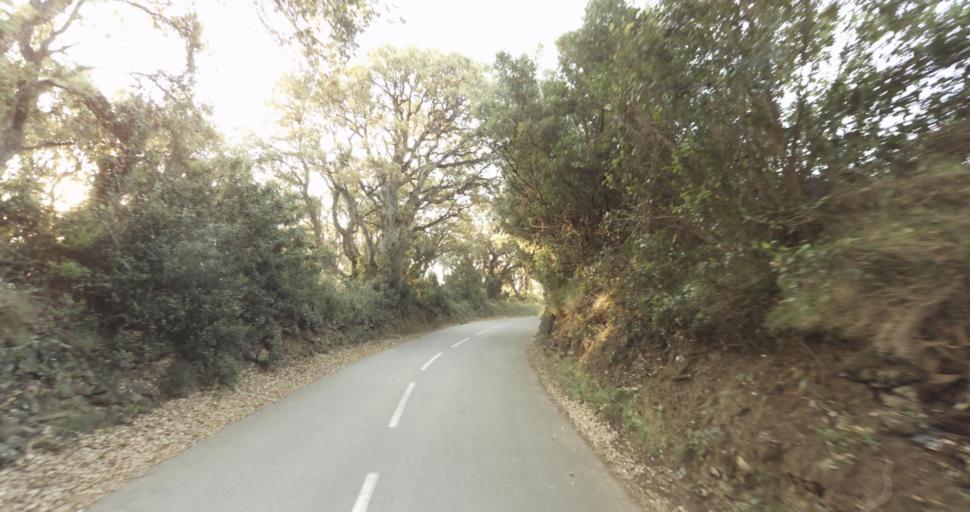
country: FR
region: Corsica
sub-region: Departement de la Haute-Corse
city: Biguglia
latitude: 42.6240
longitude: 9.4431
